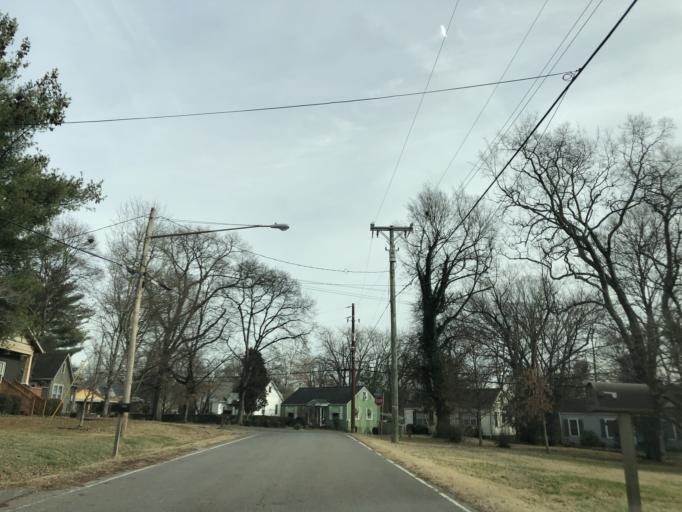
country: US
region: Tennessee
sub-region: Davidson County
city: Nashville
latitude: 36.2111
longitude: -86.7241
